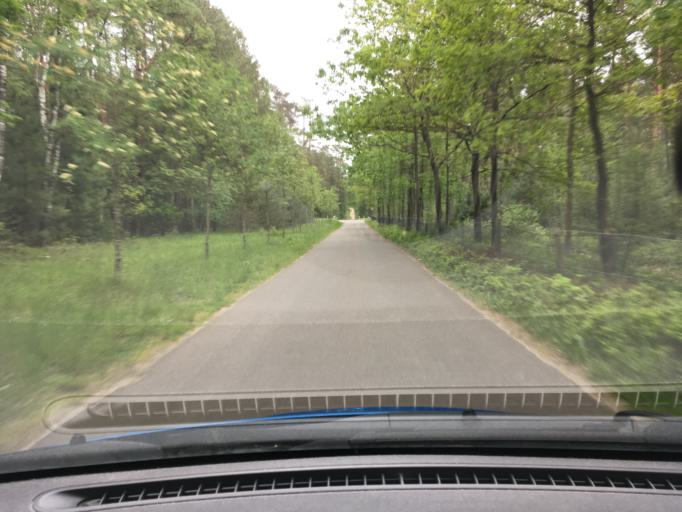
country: DE
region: Lower Saxony
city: Bispingen
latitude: 53.0716
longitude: 10.0177
